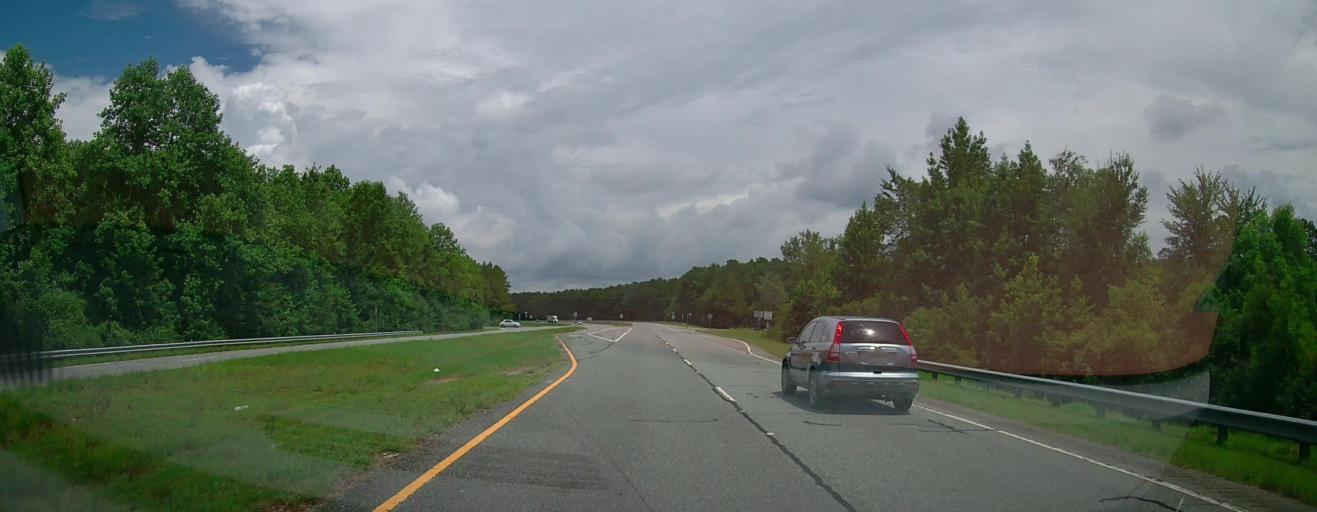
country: US
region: Georgia
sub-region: Dodge County
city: Eastman
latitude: 32.1817
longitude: -83.1938
